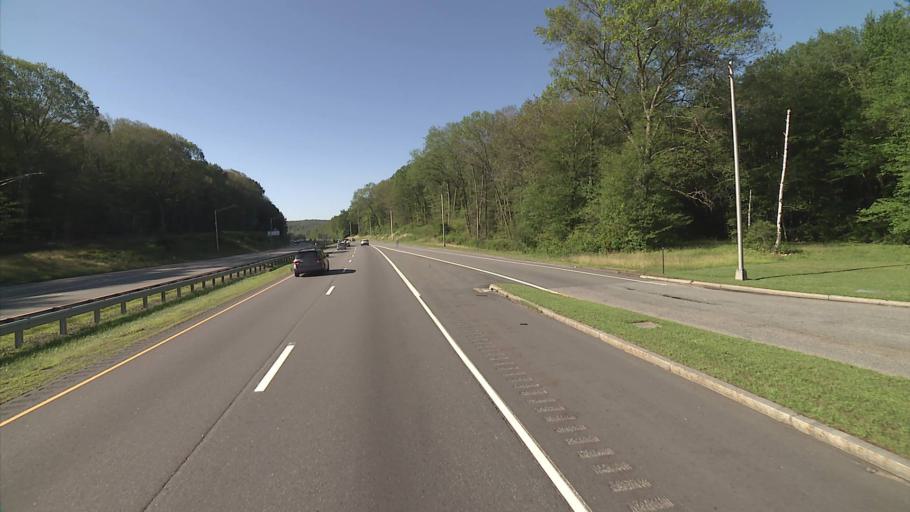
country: US
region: Connecticut
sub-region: New London County
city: Oxoboxo River
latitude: 41.4721
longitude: -72.1168
